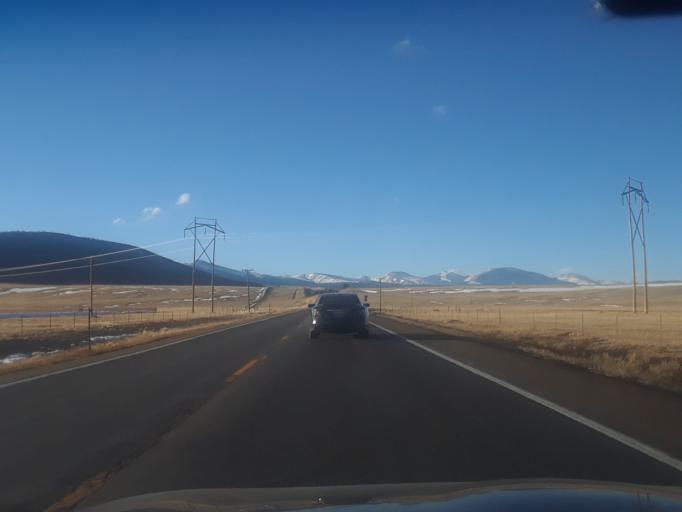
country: US
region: Colorado
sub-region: Park County
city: Fairplay
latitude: 39.0835
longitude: -105.9774
